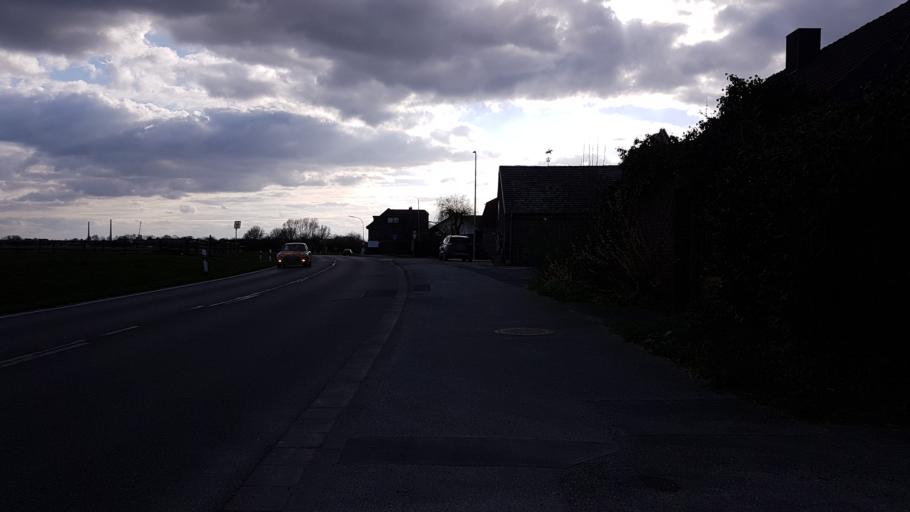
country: DE
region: North Rhine-Westphalia
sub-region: Regierungsbezirk Dusseldorf
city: Bruggen
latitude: 51.2233
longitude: 6.1989
